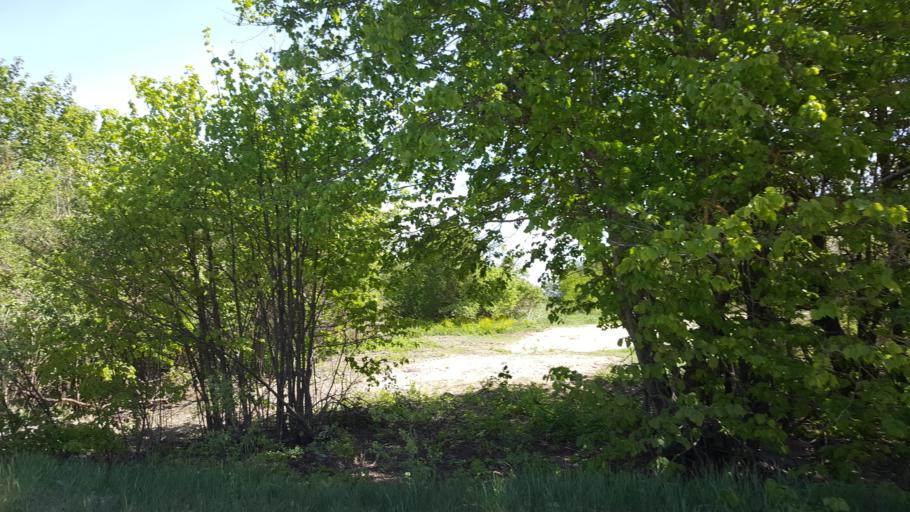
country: BY
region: Brest
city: Zhabinka
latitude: 52.3561
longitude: 24.1551
